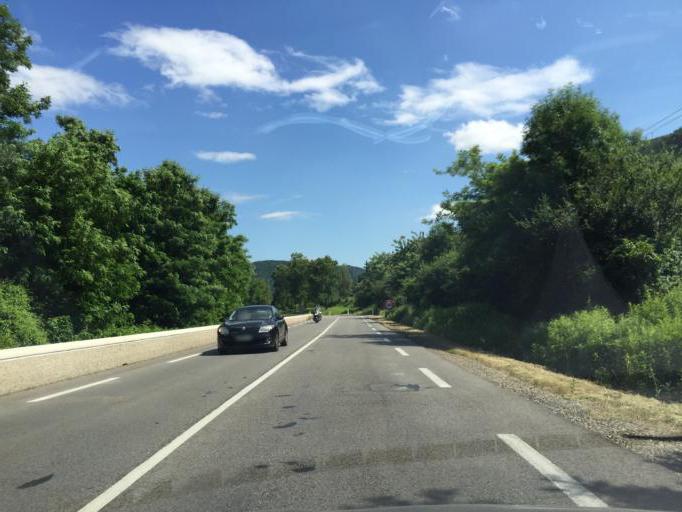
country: FR
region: Rhone-Alpes
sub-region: Departement de la Drome
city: Saint-Vallier
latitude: 45.1637
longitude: 4.8095
